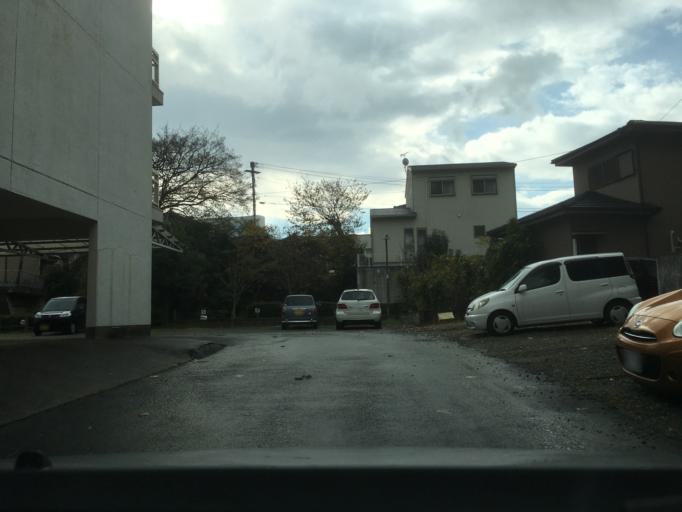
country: JP
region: Fukuoka
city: Kurume
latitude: 33.3241
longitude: 130.5083
